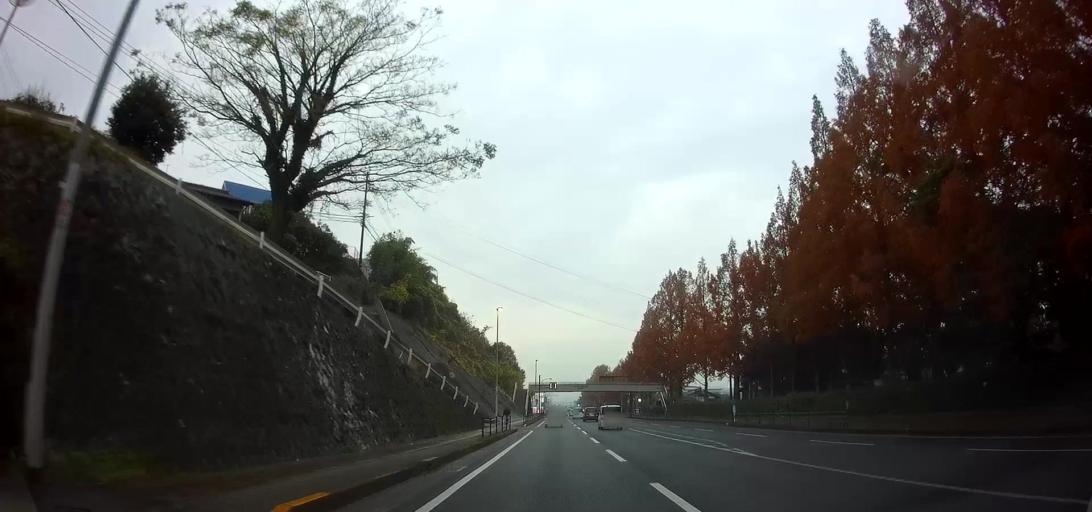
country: JP
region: Nagasaki
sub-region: Isahaya-shi
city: Isahaya
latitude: 32.8361
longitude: 130.0392
